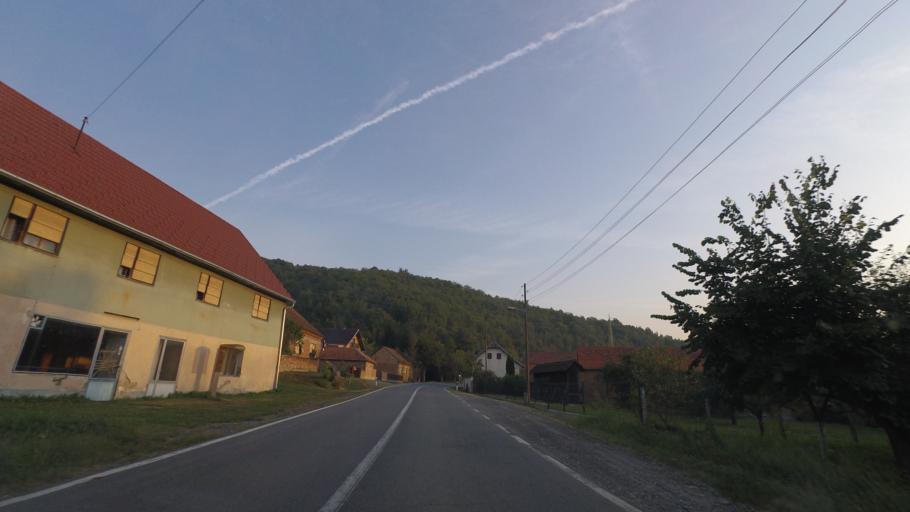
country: HR
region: Brodsko-Posavska
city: Resetari
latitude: 45.3373
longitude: 17.4562
